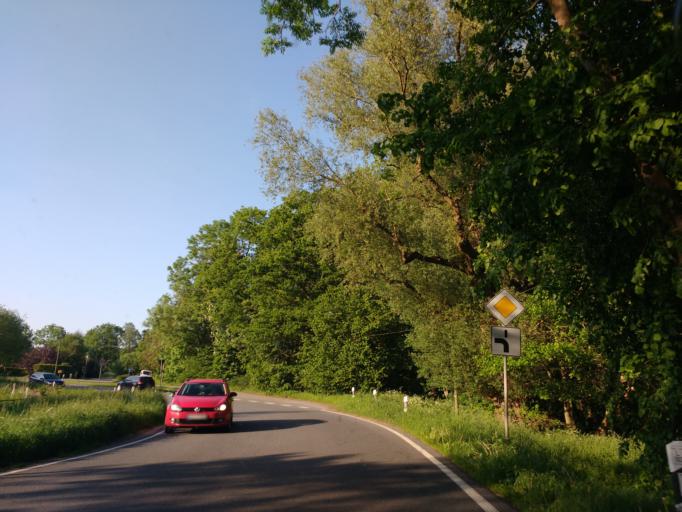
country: DE
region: Mecklenburg-Vorpommern
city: Lubow
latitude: 53.8674
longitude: 11.5320
